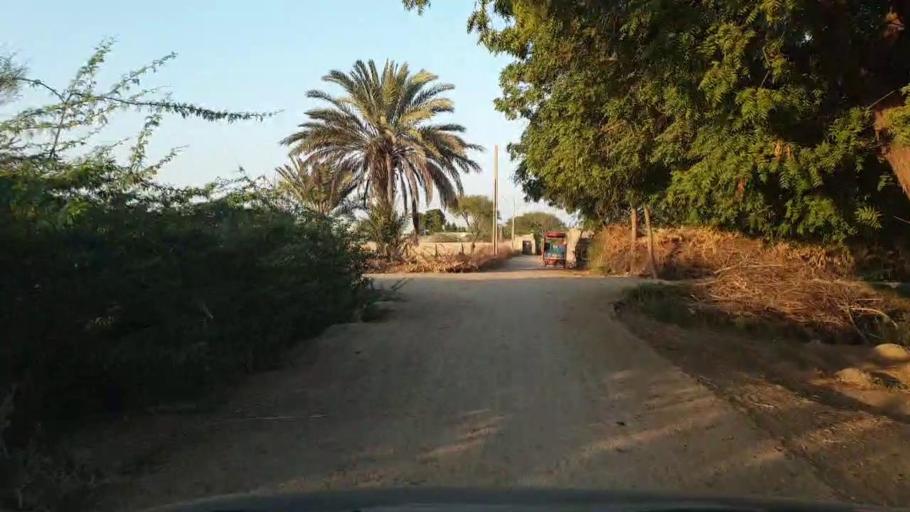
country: PK
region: Sindh
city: Digri
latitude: 25.1114
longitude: 69.2401
